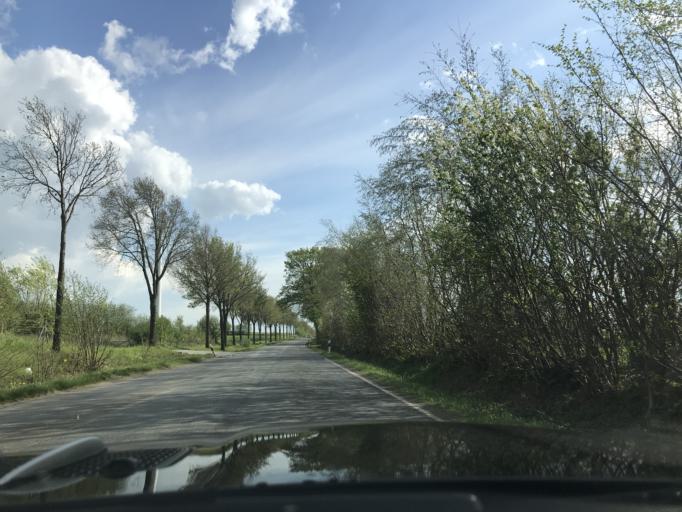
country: DE
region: Schleswig-Holstein
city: Woltersdorf
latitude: 53.5878
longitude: 10.6409
